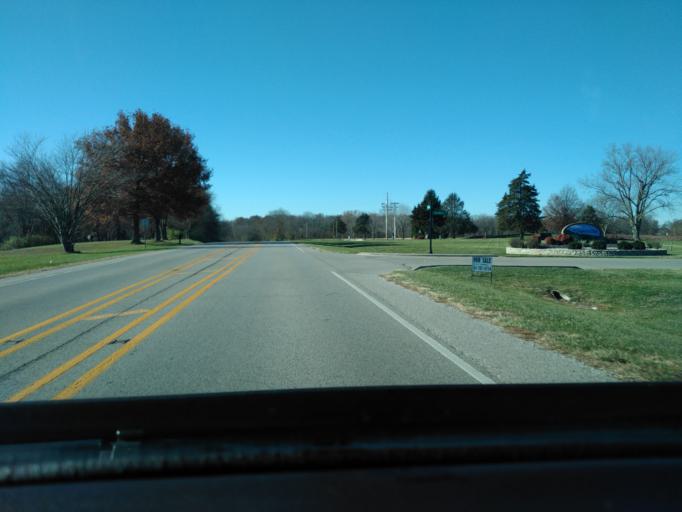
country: US
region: Illinois
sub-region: Madison County
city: Highland
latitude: 38.7734
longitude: -89.6432
